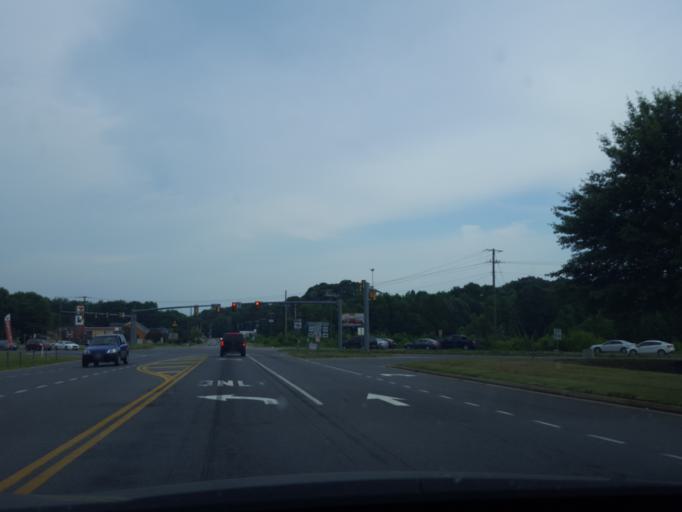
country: US
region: Virginia
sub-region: King George County
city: Dahlgren
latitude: 38.3400
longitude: -77.0768
